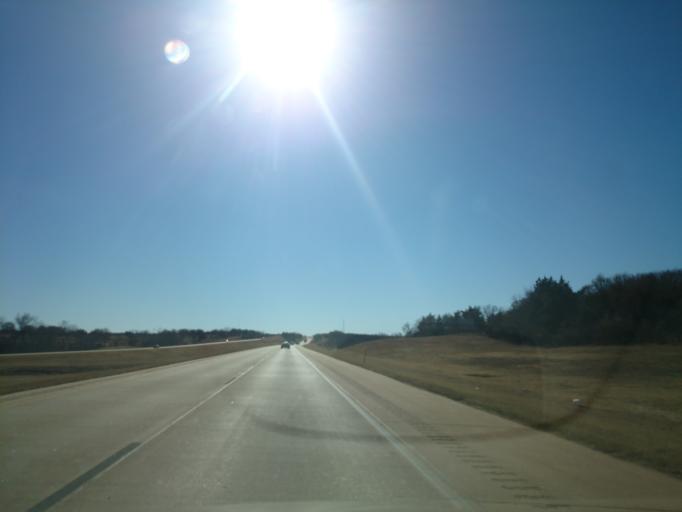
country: US
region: Oklahoma
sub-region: Logan County
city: Guthrie
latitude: 35.7803
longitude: -97.4166
